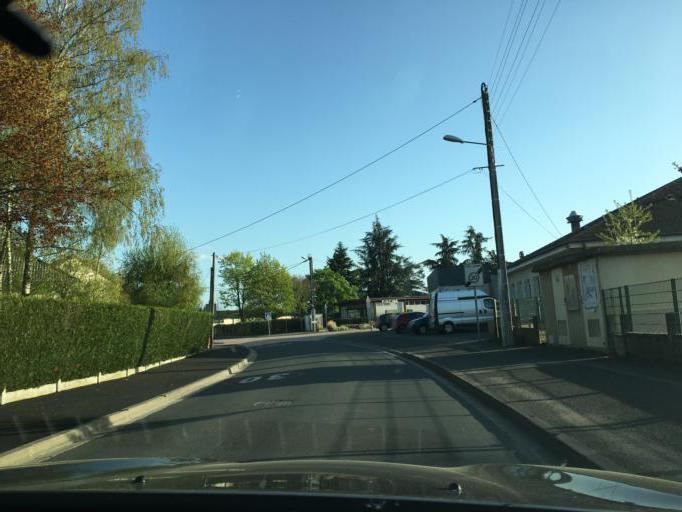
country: FR
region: Centre
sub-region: Departement du Loir-et-Cher
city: Ouzouer-le-Marche
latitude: 47.9091
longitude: 1.5313
